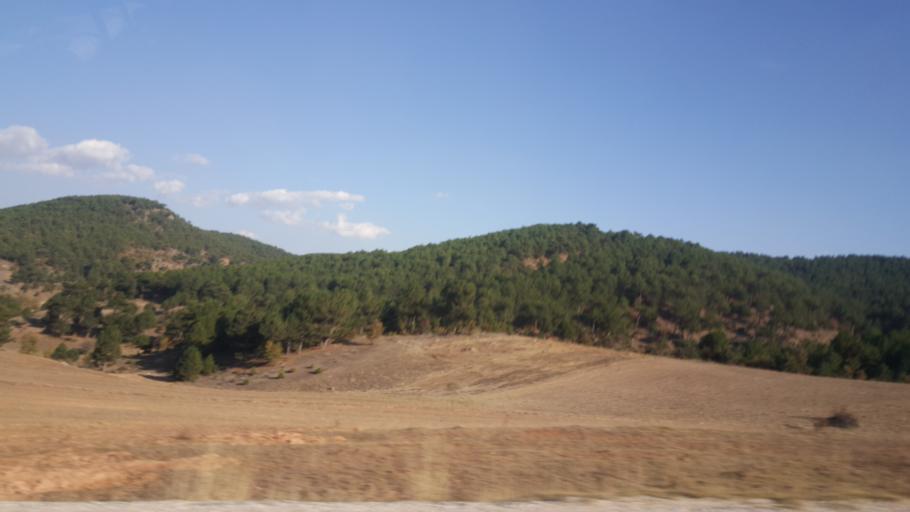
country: TR
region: Eskisehir
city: Kirka
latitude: 39.1201
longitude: 30.5897
